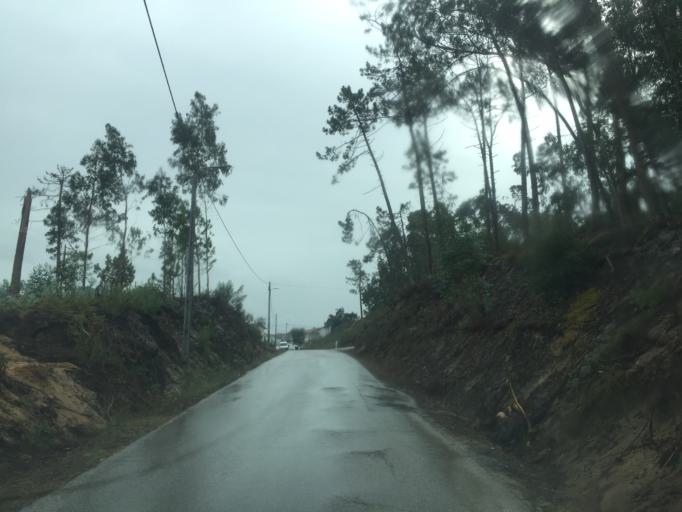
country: PT
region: Coimbra
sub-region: Figueira da Foz
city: Lavos
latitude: 40.0638
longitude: -8.7754
